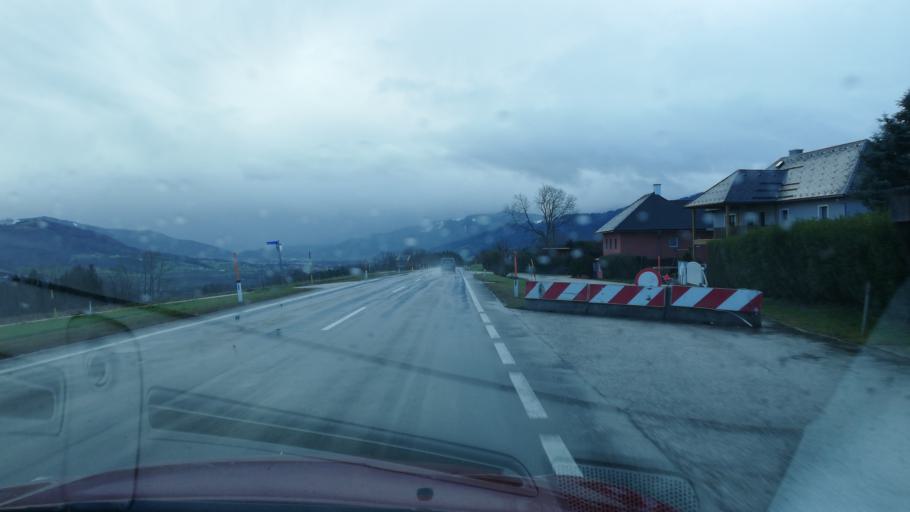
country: AT
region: Upper Austria
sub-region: Politischer Bezirk Kirchdorf an der Krems
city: Kremsmunster
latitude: 47.9684
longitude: 14.0790
